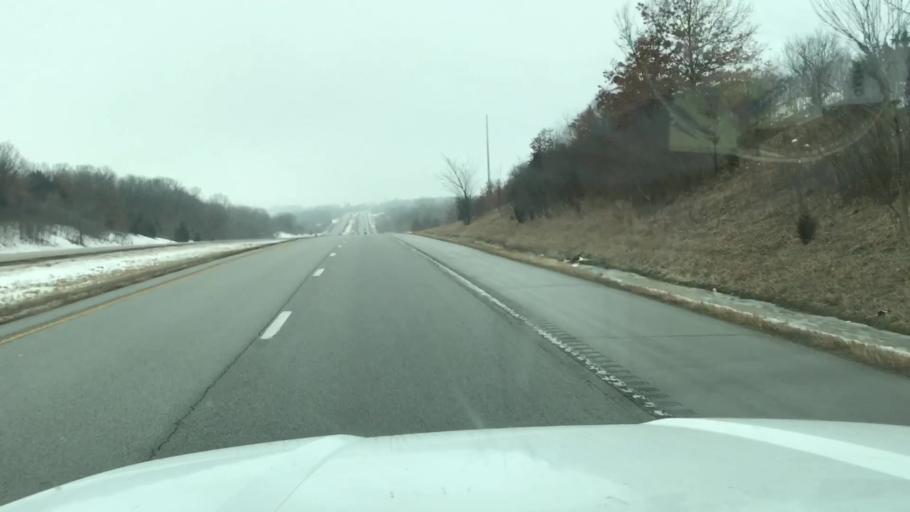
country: US
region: Missouri
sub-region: Clinton County
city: Gower
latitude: 39.7541
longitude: -94.5877
